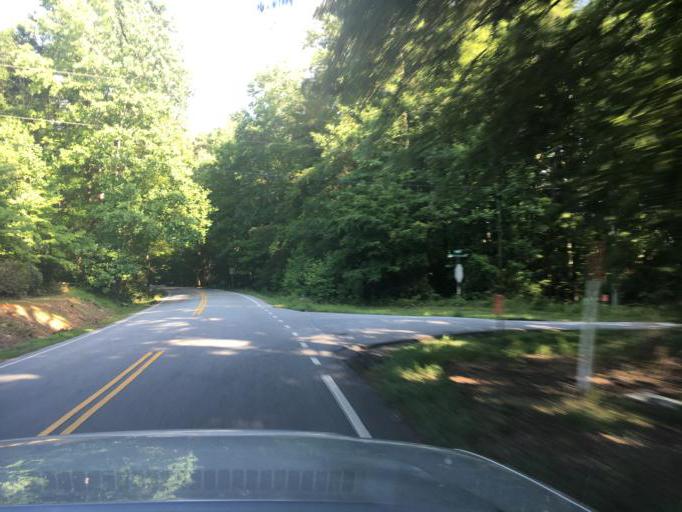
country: US
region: South Carolina
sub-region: Greenville County
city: Simpsonville
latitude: 34.7705
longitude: -82.2644
